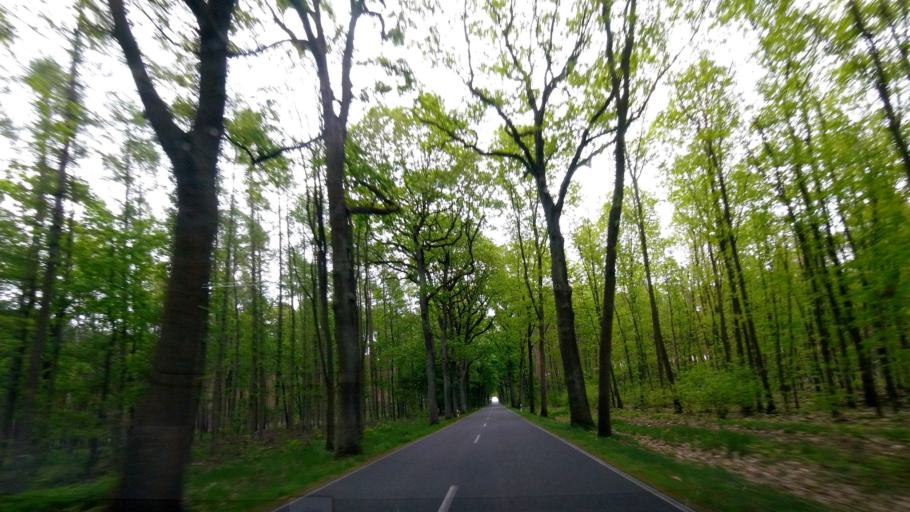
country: DE
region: Brandenburg
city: Ihlow
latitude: 51.9205
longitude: 13.3851
